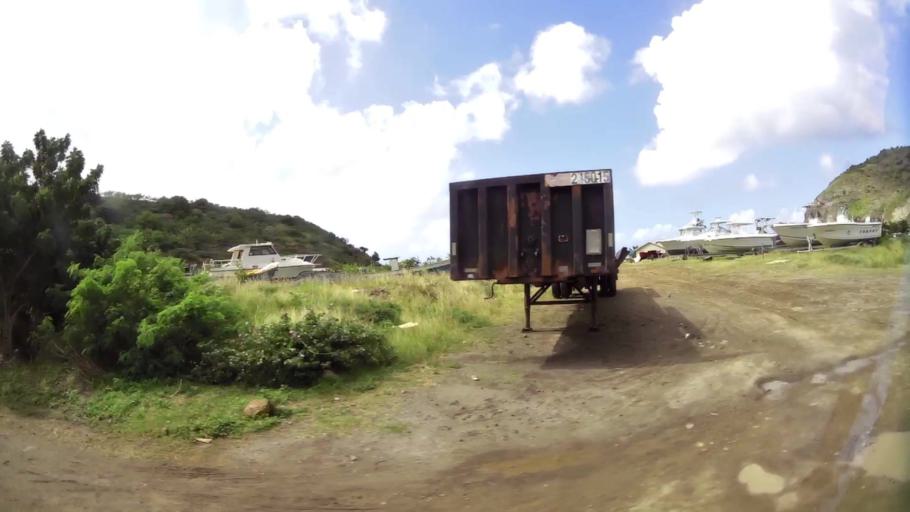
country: MS
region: Saint Peter
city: Brades
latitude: 16.8005
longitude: -62.2042
